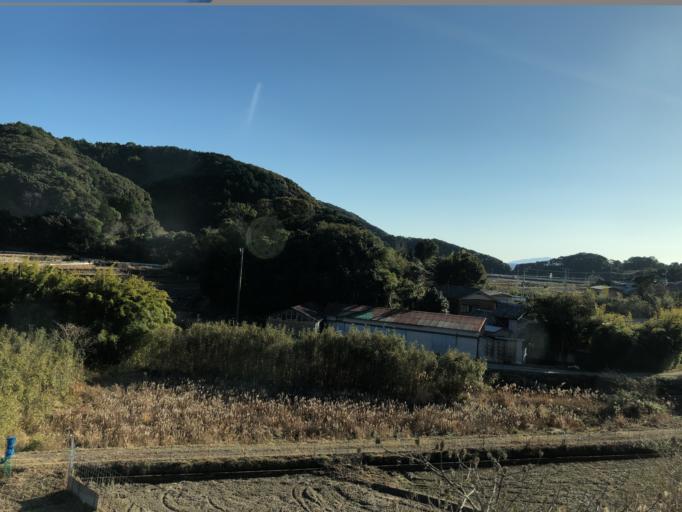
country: JP
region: Kochi
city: Nakamura
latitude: 33.0399
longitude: 133.0809
